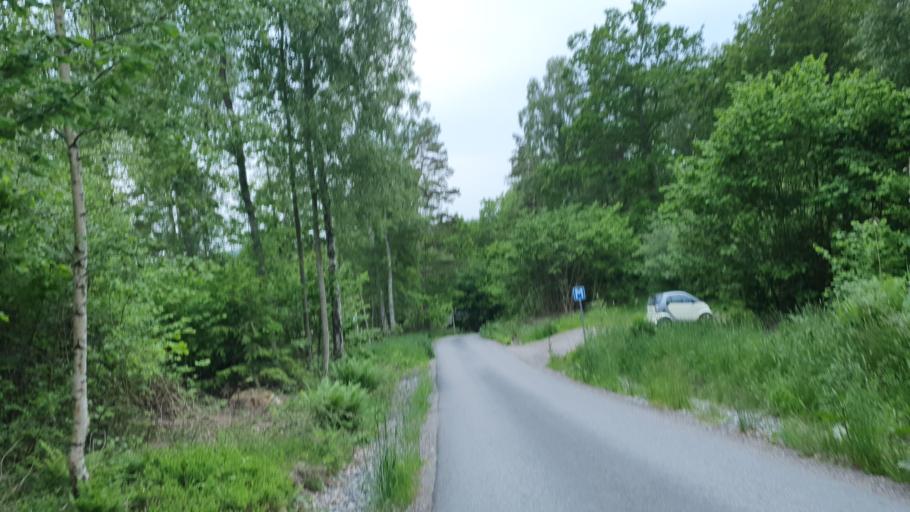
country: SE
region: Vaestra Goetaland
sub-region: Molndal
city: Kallered
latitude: 57.6140
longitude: 12.0580
